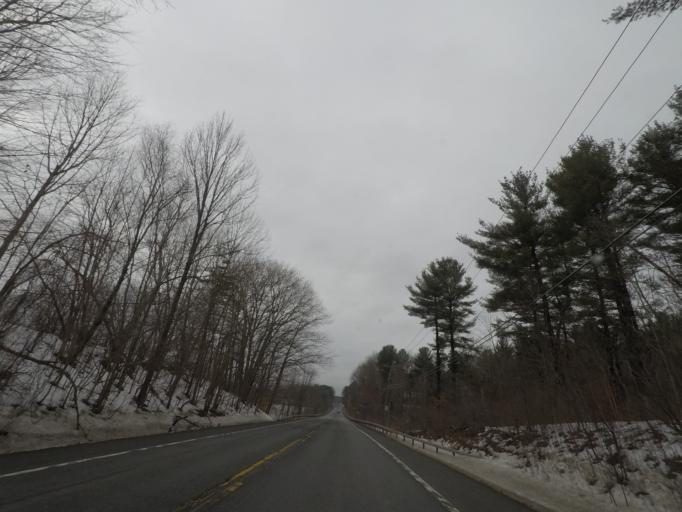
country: US
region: New York
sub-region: Schenectady County
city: Rotterdam
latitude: 42.7315
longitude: -73.9755
